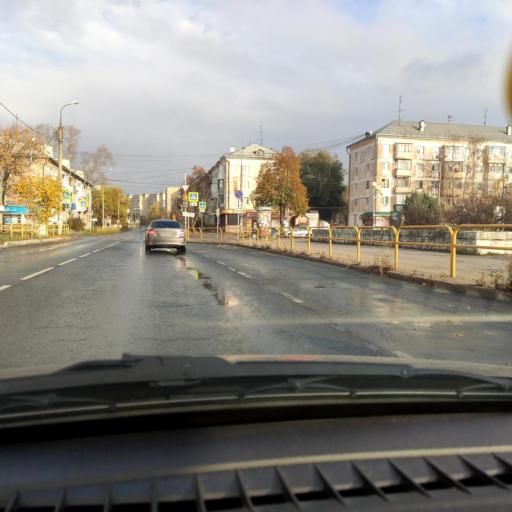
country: RU
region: Samara
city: Tol'yatti
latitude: 53.5035
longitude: 49.4004
